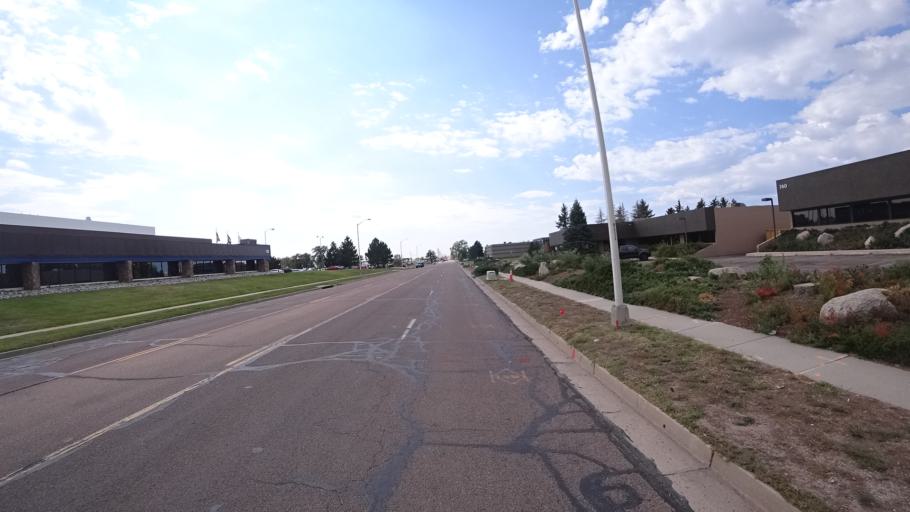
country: US
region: Colorado
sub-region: El Paso County
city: Cimarron Hills
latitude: 38.8438
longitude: -104.7388
